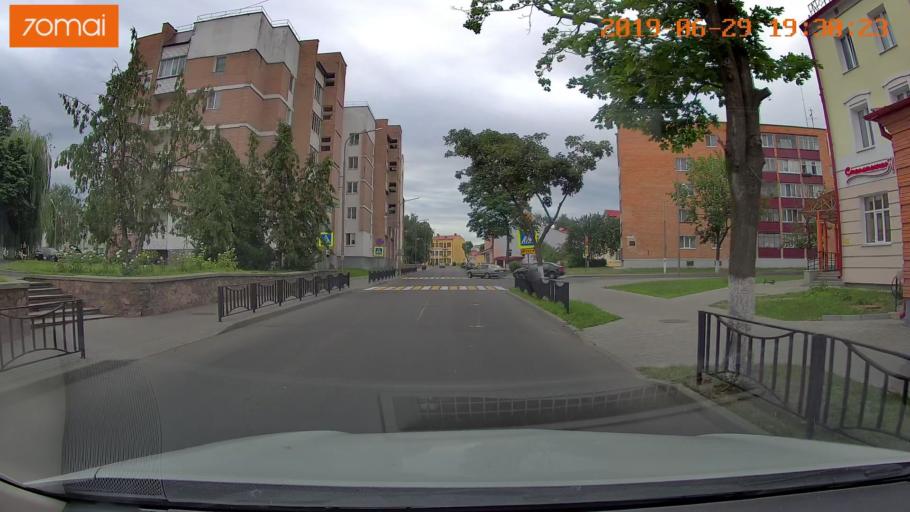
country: BY
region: Brest
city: Pinsk
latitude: 52.1154
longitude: 26.1121
